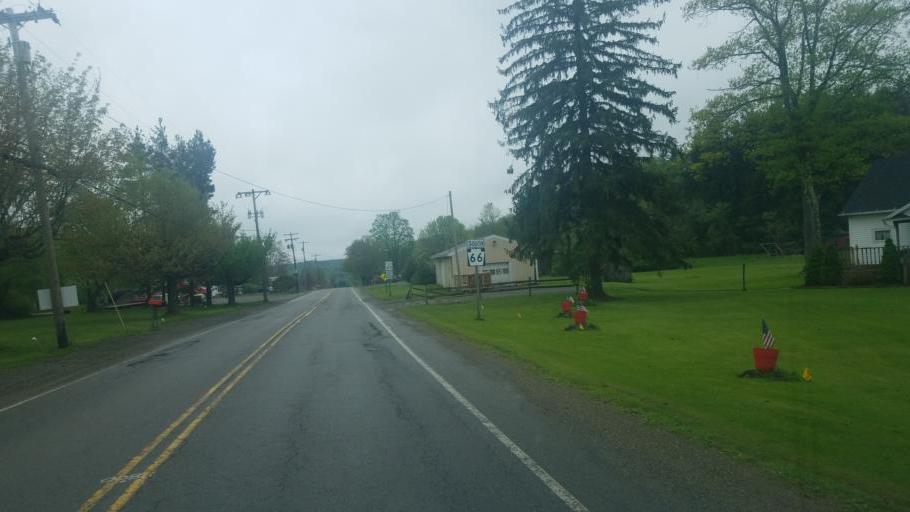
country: US
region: Pennsylvania
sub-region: McKean County
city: Kane
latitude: 41.6463
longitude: -78.8138
